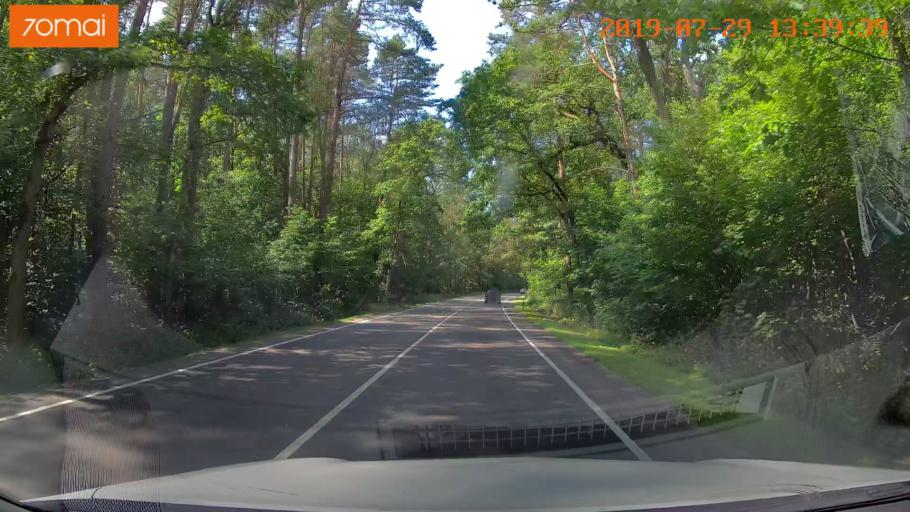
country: RU
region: Kaliningrad
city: Svetlyy
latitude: 54.7244
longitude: 20.1495
